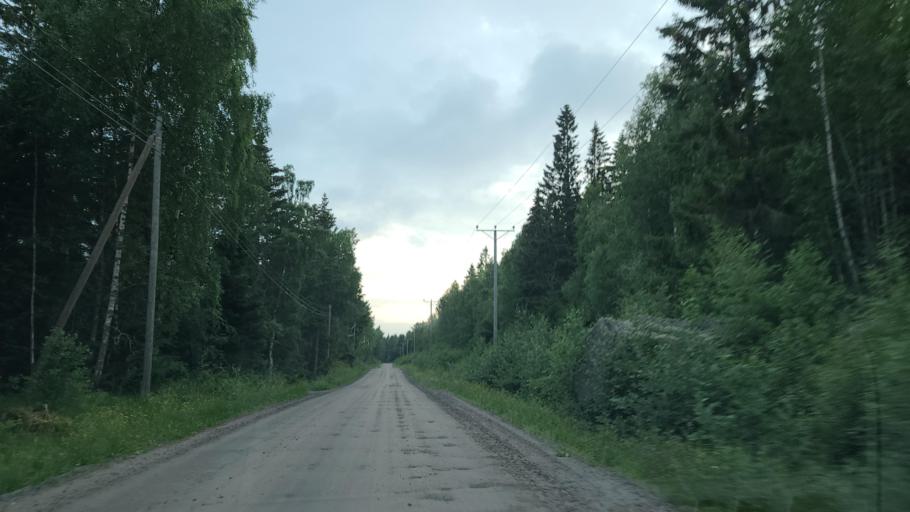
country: FI
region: Ostrobothnia
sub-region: Vaasa
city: Replot
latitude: 63.2988
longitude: 21.1354
